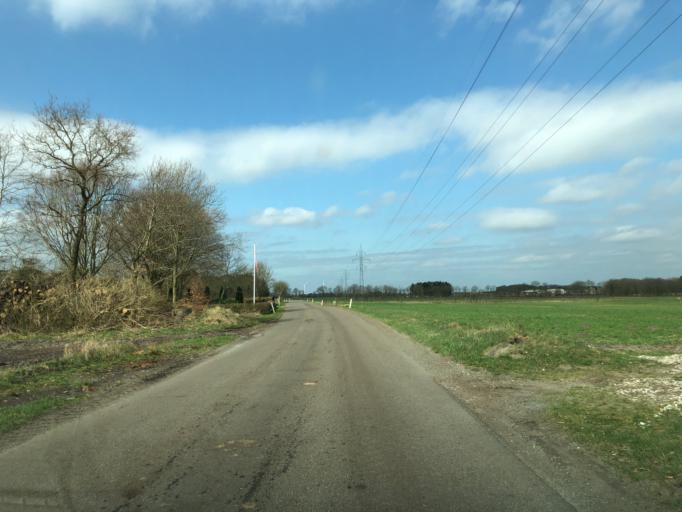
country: DK
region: South Denmark
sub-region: Vejle Kommune
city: Give
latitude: 55.9150
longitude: 9.2254
